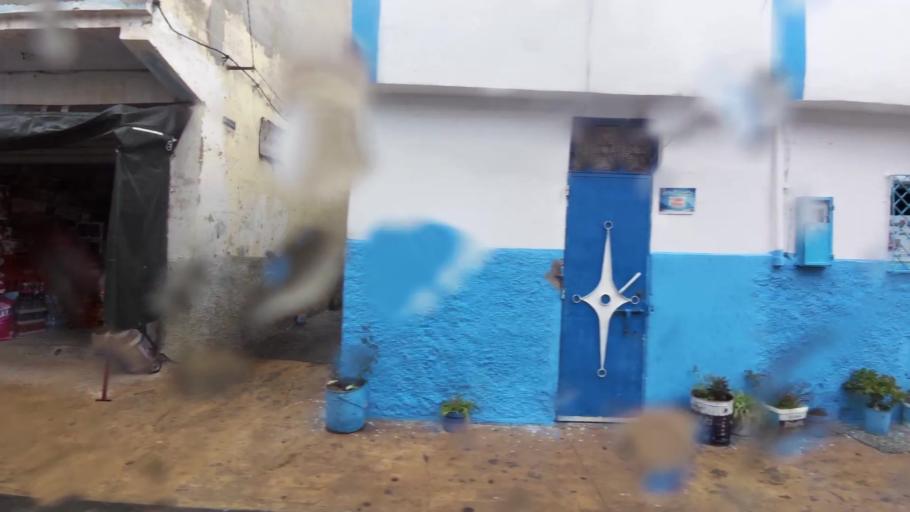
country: MA
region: Tanger-Tetouan
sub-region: Tetouan
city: Martil
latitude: 35.6213
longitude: -5.2807
